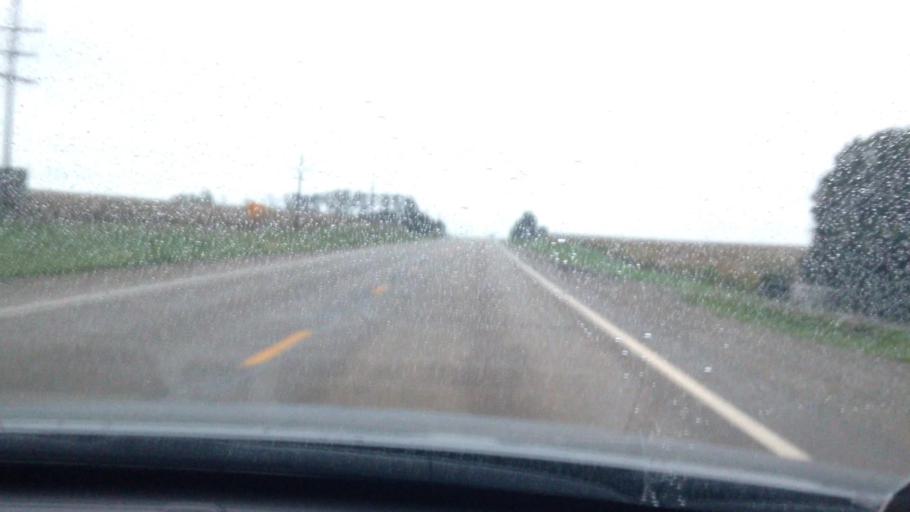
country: US
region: Kansas
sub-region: Brown County
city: Hiawatha
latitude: 39.8202
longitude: -95.5272
